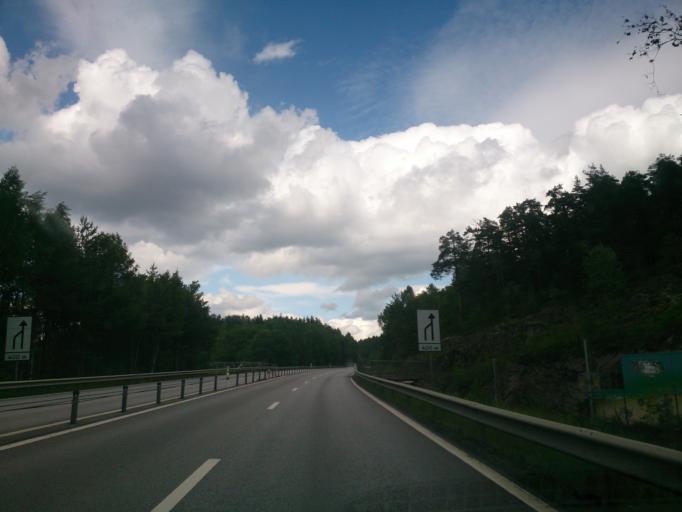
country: SE
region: OEstergoetland
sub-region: Norrkopings Kommun
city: Jursla
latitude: 58.6869
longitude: 16.1516
